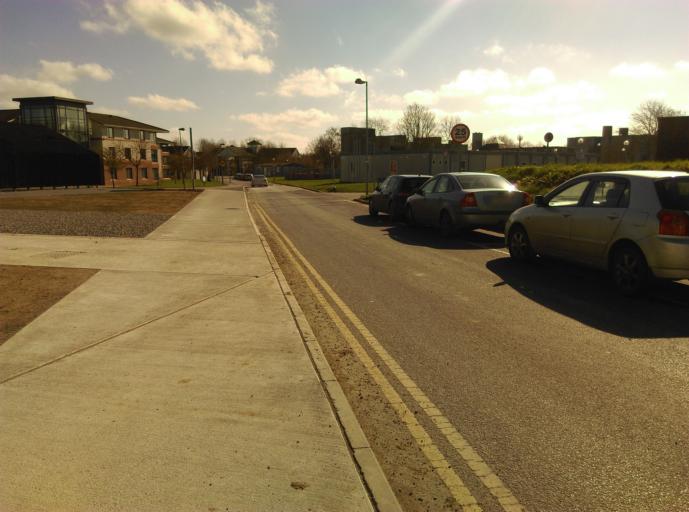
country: IE
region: Leinster
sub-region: Kildare
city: Maynooth
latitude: 53.3857
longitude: -6.6013
